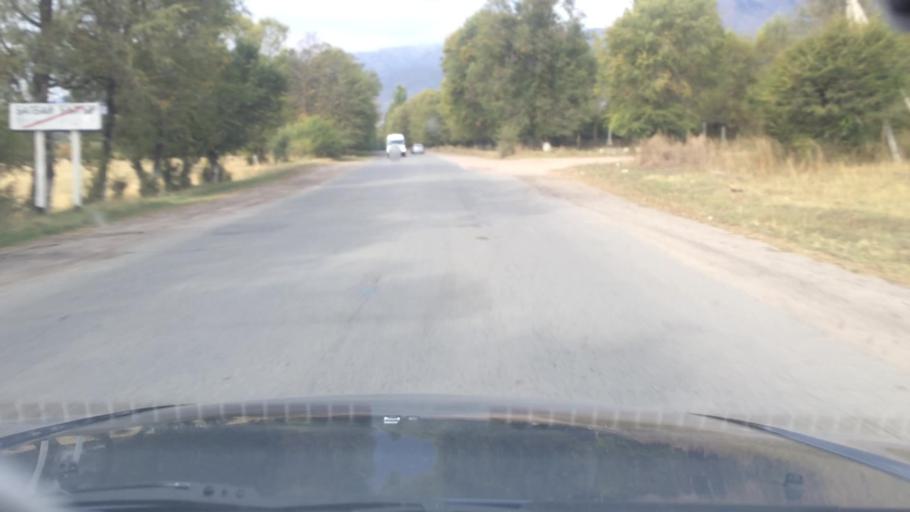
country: KG
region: Ysyk-Koel
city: Tyup
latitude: 42.7846
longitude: 78.2752
